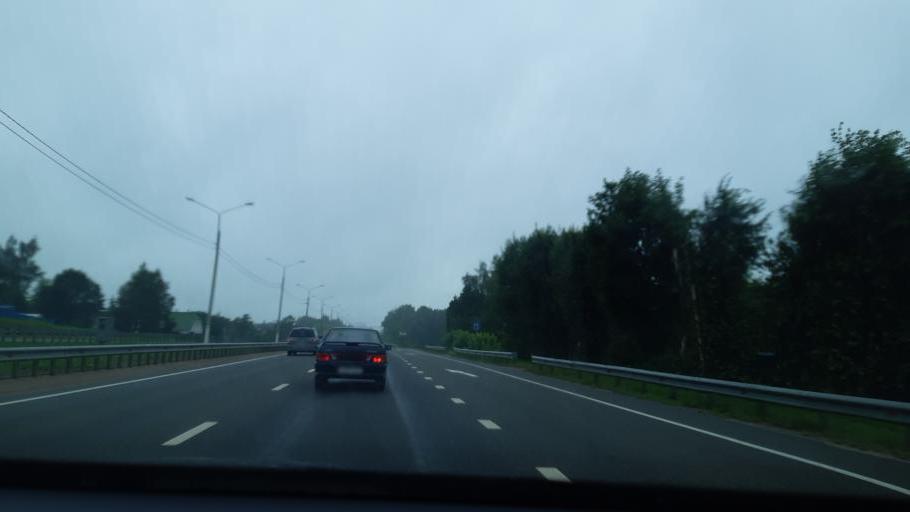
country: RU
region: Smolensk
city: Talashkino
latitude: 54.6739
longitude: 32.1469
